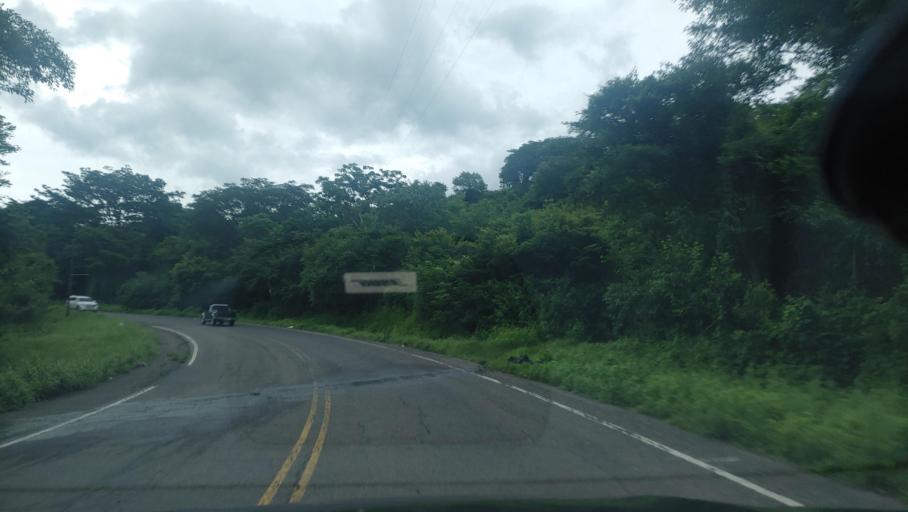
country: HN
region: Choluteca
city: Santa Ana de Yusguare
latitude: 13.3722
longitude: -87.0691
